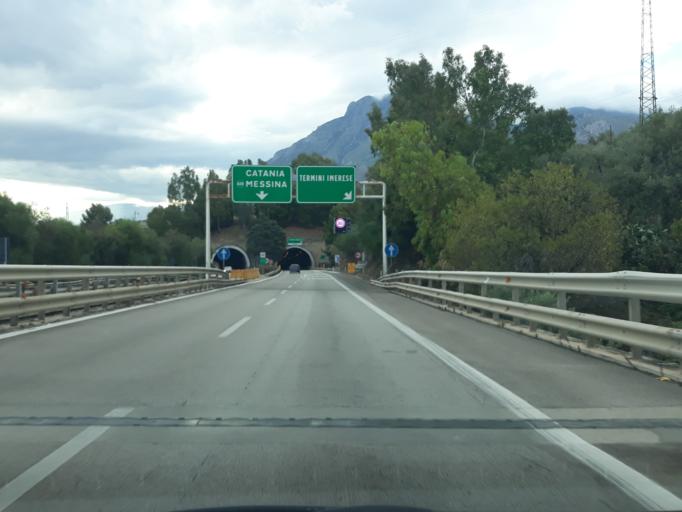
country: IT
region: Sicily
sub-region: Palermo
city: Termini Imerese
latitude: 37.9759
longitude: 13.6801
